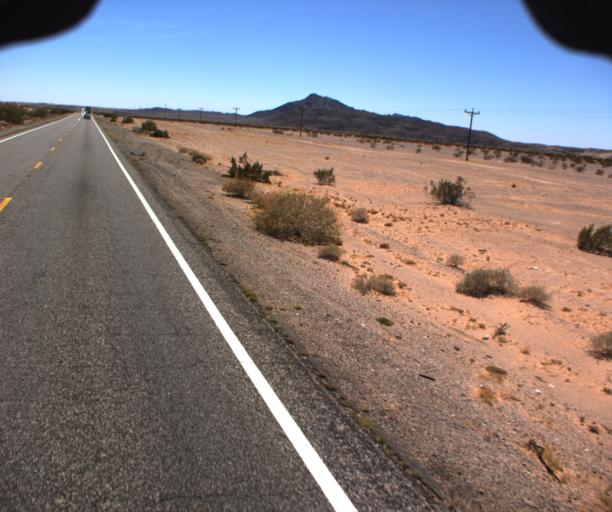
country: US
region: Arizona
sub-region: La Paz County
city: Parker
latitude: 34.0460
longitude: -114.2581
